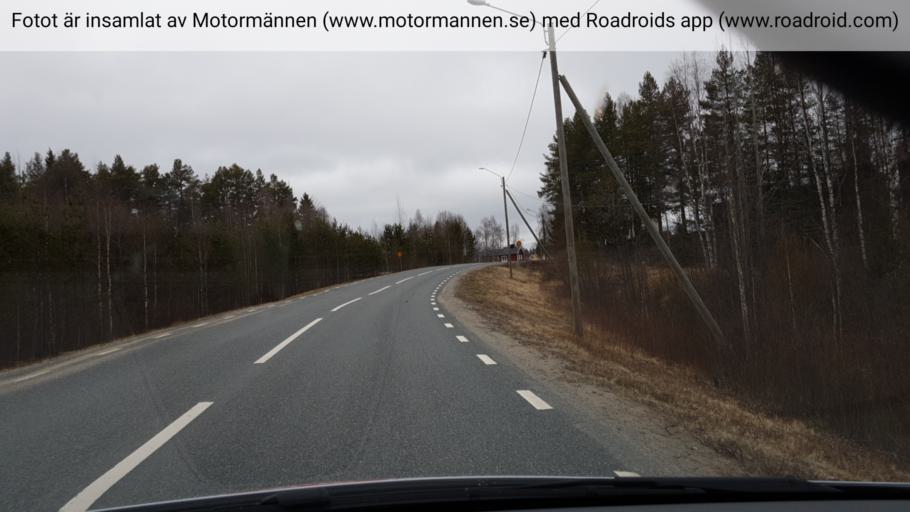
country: SE
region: Vaesternorrland
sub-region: OErnskoeldsviks Kommun
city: Bredbyn
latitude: 63.8480
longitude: 18.4707
